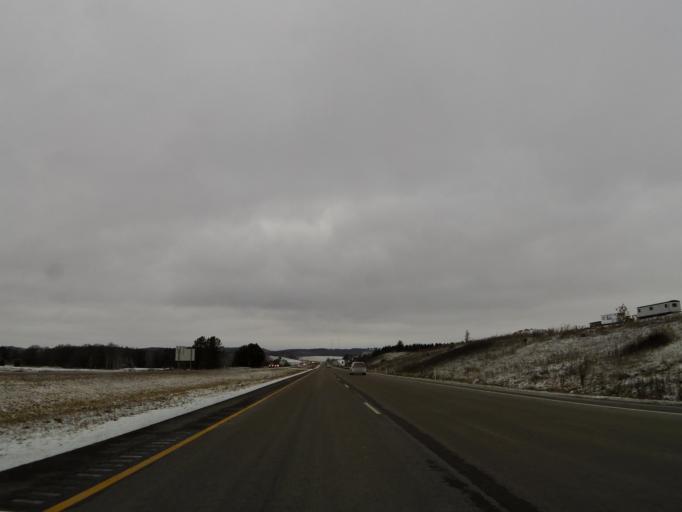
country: US
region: Wisconsin
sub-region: Trempealeau County
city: Osseo
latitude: 44.5828
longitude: -91.2076
